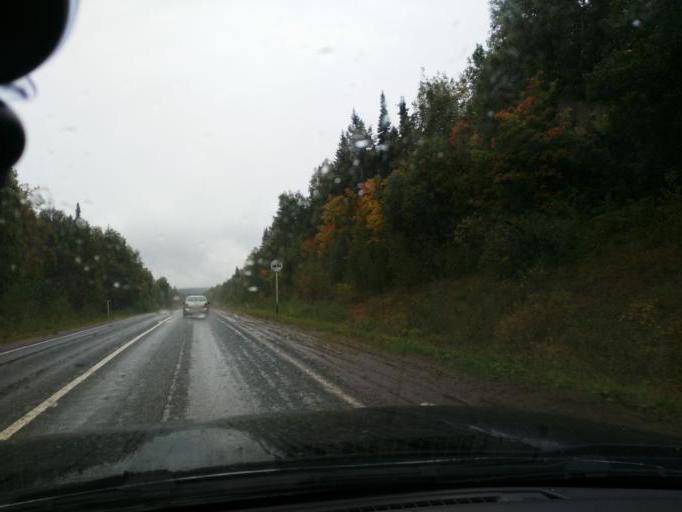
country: RU
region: Perm
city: Yugo-Kamskiy
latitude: 57.6073
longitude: 55.6506
